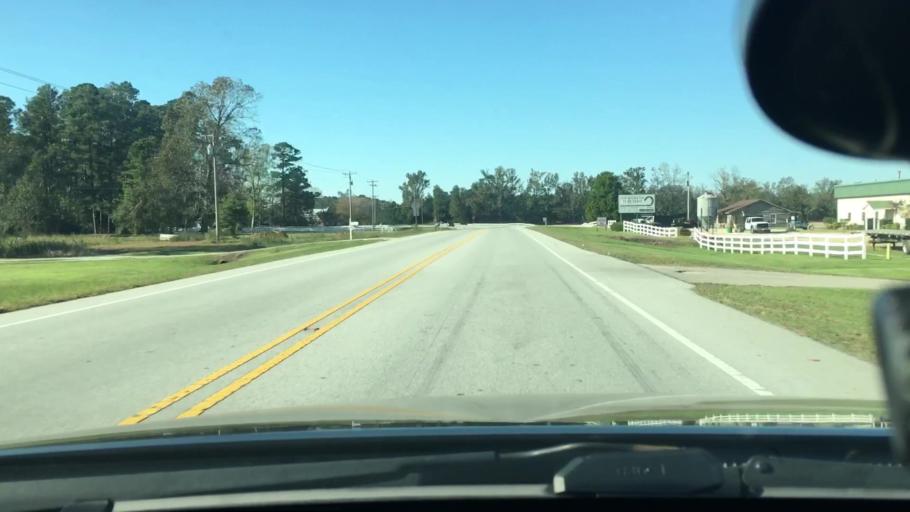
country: US
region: North Carolina
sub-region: Craven County
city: Trent Woods
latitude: 35.1621
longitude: -77.1187
